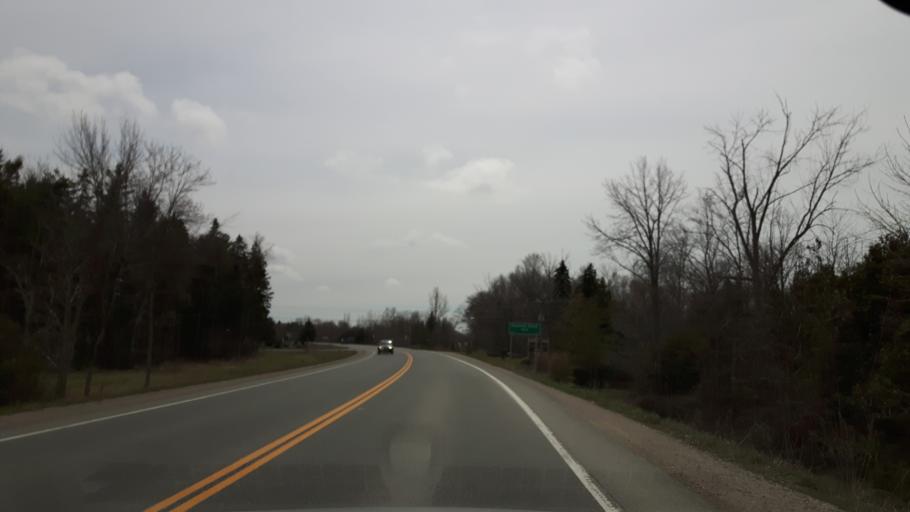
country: CA
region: Ontario
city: Bluewater
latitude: 43.5771
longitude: -81.7056
